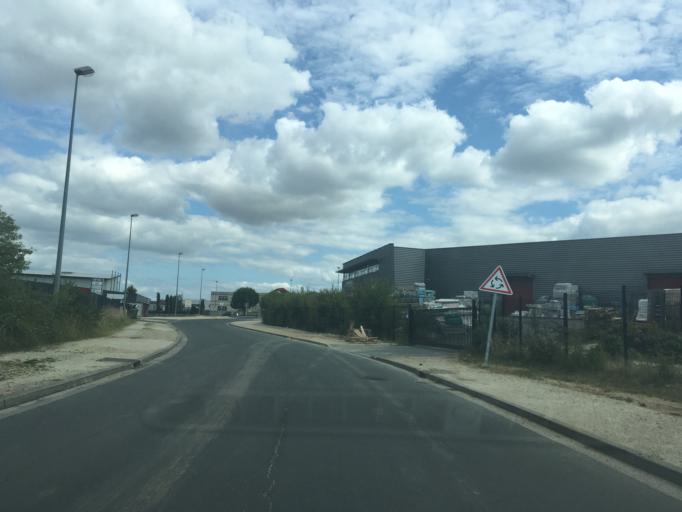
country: FR
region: Aquitaine
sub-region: Departement de la Gironde
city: Eysines
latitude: 44.8676
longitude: -0.6561
